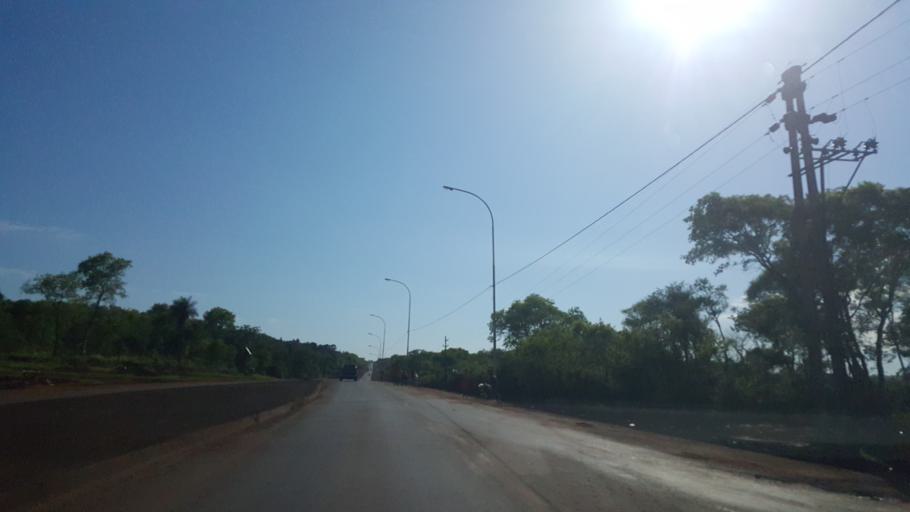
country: AR
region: Misiones
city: Santa Ana
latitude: -27.3766
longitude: -55.5753
